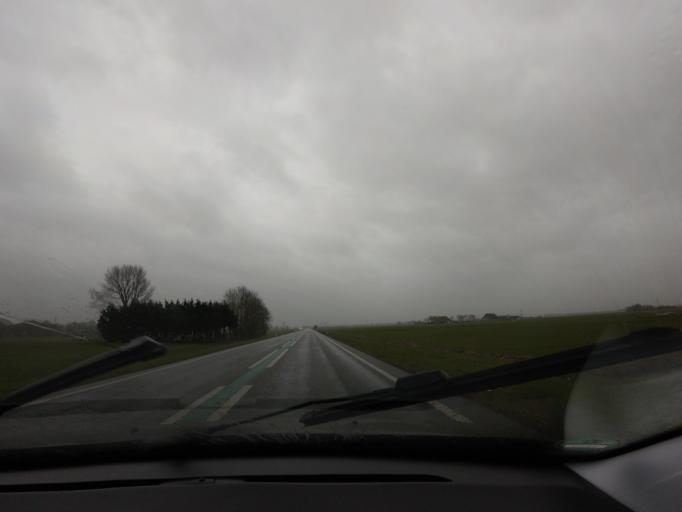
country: NL
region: Friesland
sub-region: Sudwest Fryslan
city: Bolsward
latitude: 53.0835
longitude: 5.5215
